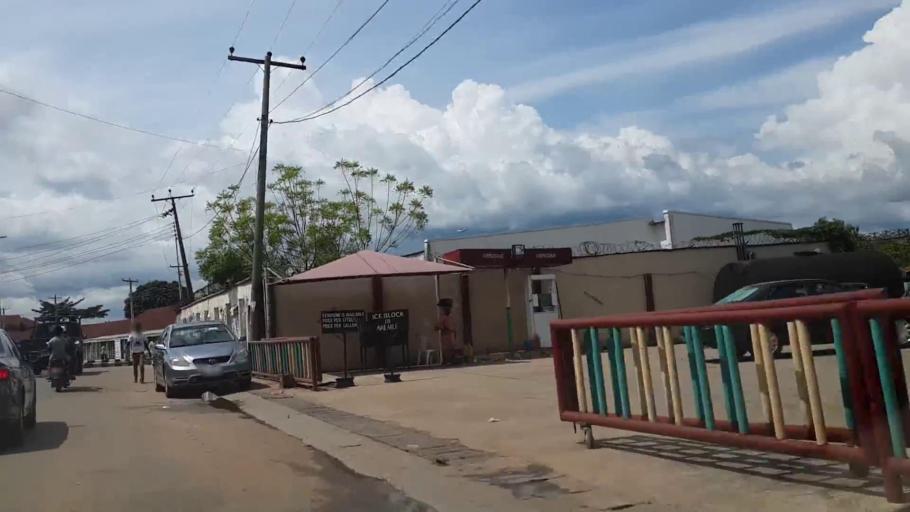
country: NG
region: Ondo
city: Ondo
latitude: 7.0977
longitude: 4.8413
